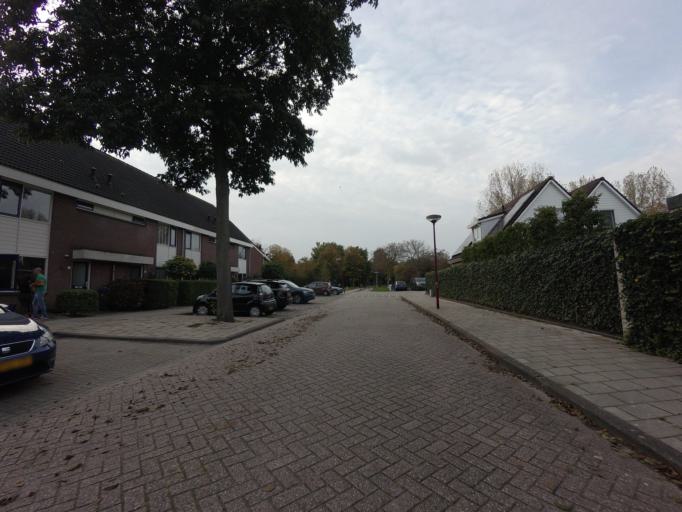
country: NL
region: Utrecht
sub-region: Gemeente Nieuwegein
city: Nieuwegein
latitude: 52.0490
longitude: 5.0688
